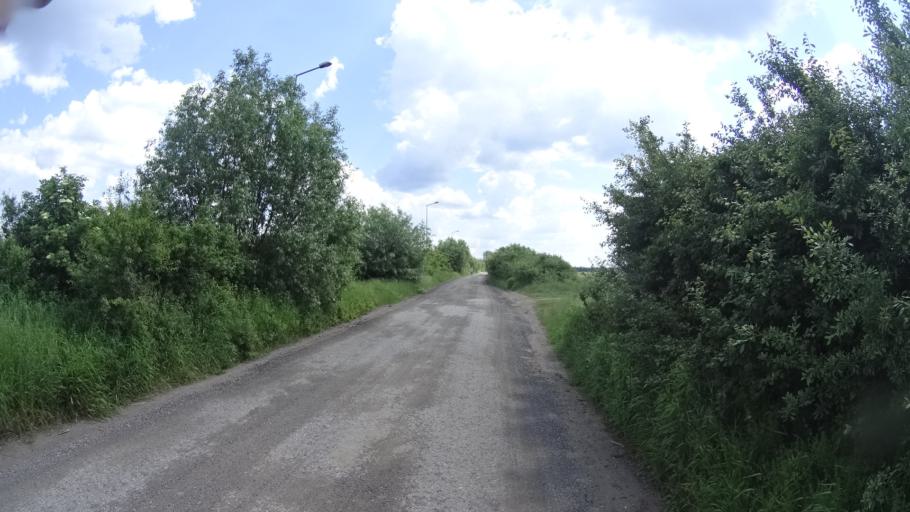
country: PL
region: Masovian Voivodeship
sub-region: Powiat pruszkowski
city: Nadarzyn
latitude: 52.0573
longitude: 20.8236
